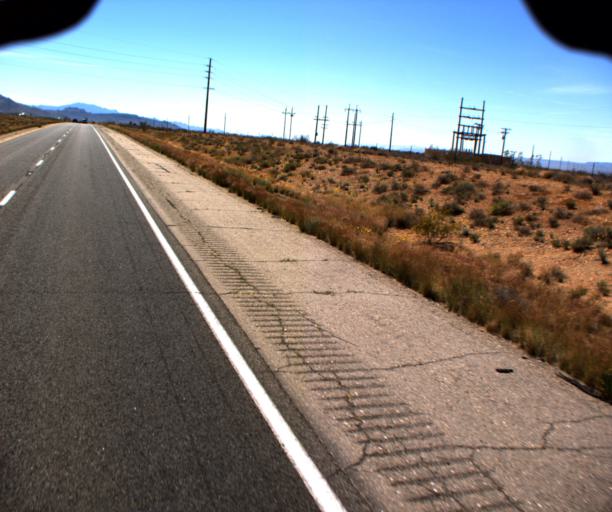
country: US
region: Arizona
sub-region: Mohave County
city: Golden Valley
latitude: 35.3204
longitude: -114.2043
